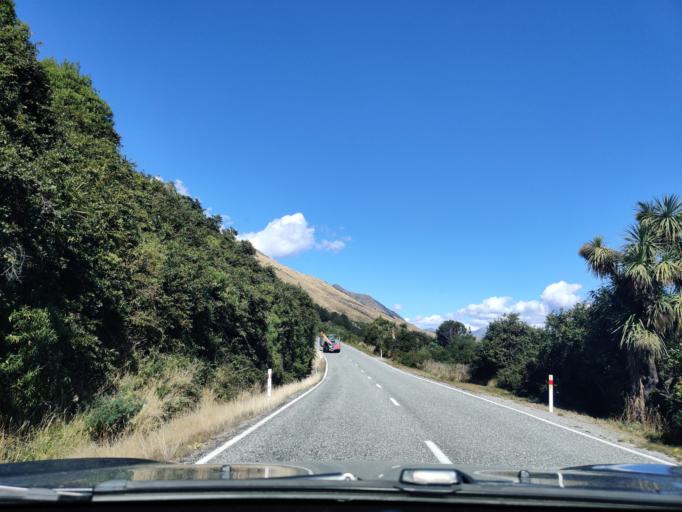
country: NZ
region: Otago
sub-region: Queenstown-Lakes District
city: Queenstown
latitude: -44.9495
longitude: 168.4353
